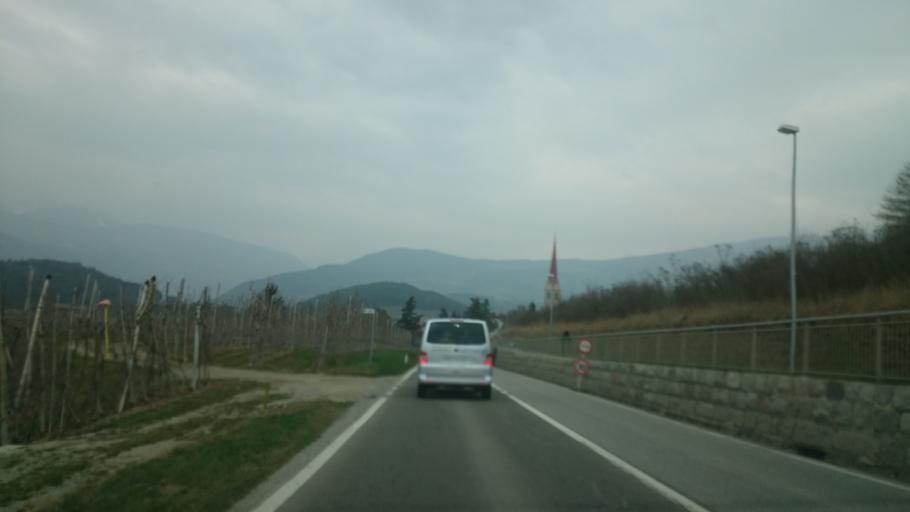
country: IT
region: Trentino-Alto Adige
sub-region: Bolzano
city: Naz-Sciaves - Natz-Schabs
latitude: 46.7672
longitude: 11.6622
